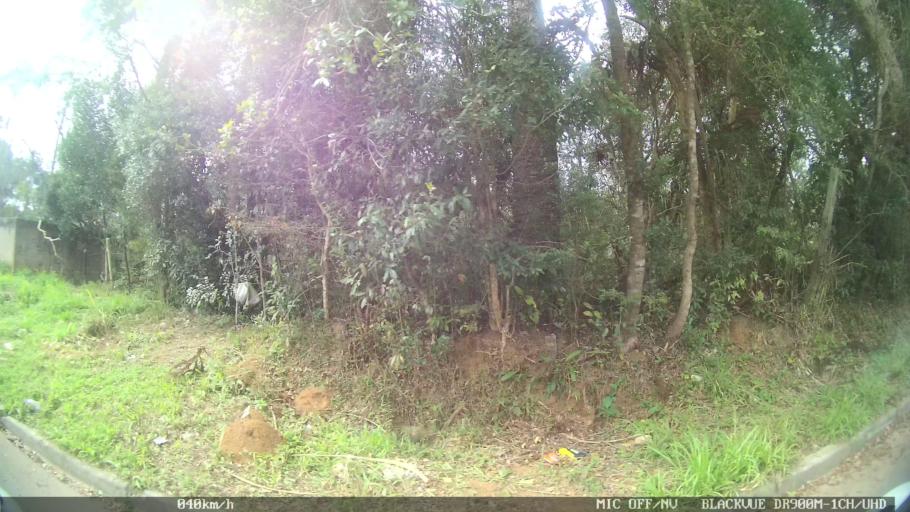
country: BR
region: Parana
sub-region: Colombo
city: Colombo
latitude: -25.3512
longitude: -49.2306
